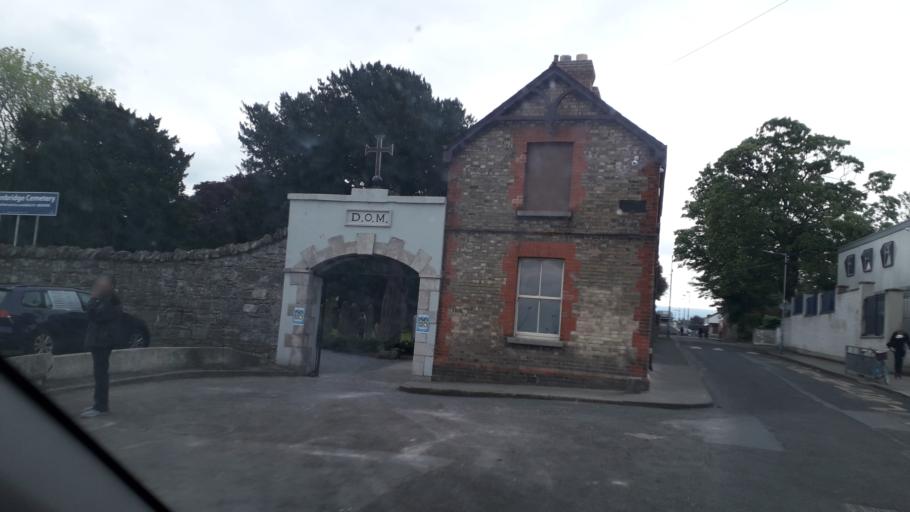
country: IE
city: Greenhills
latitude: 53.3368
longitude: -6.3179
